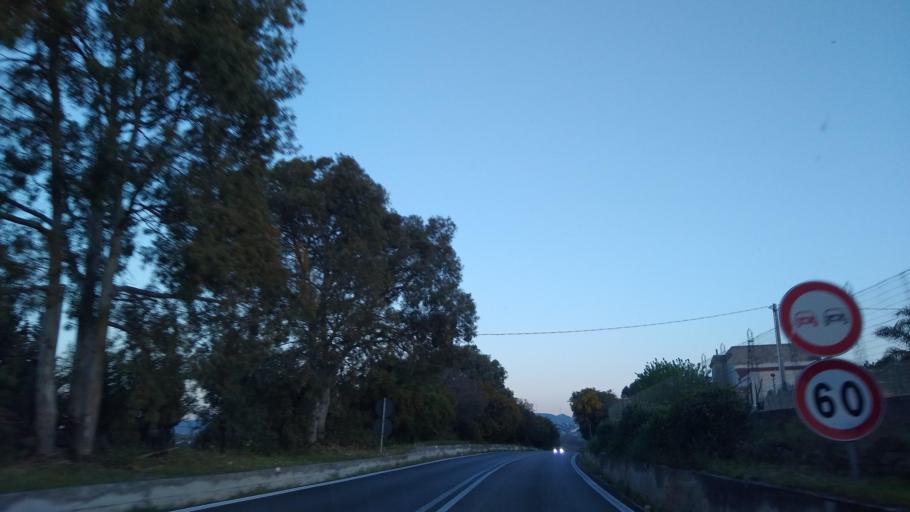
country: IT
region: Sicily
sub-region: Trapani
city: Alcamo
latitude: 38.0136
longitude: 12.9601
